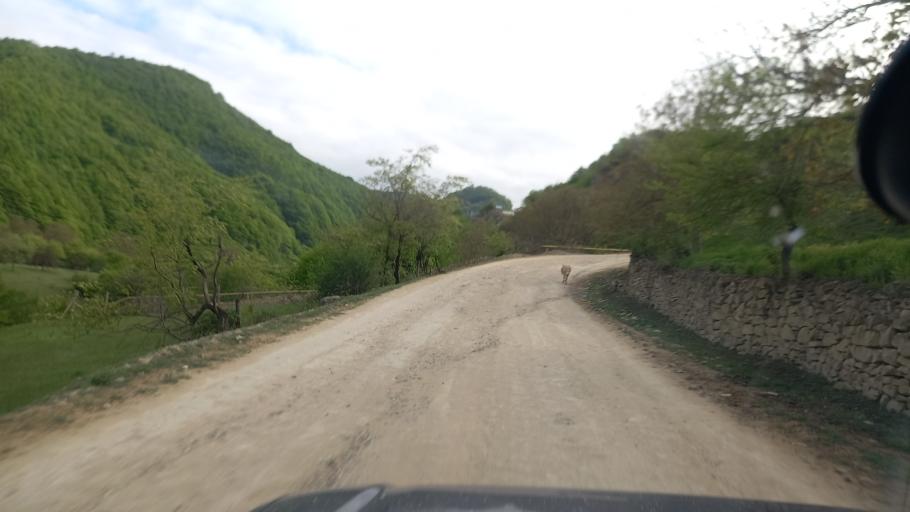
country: RU
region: Dagestan
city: Khuchni
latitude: 41.9687
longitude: 47.8761
